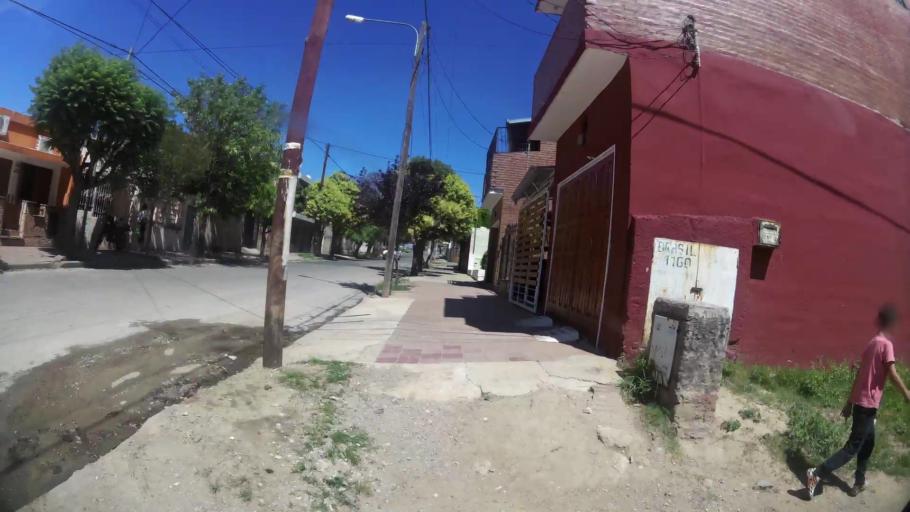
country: AR
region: Cordoba
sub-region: Departamento de Capital
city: Cordoba
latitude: -31.4255
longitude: -64.2046
